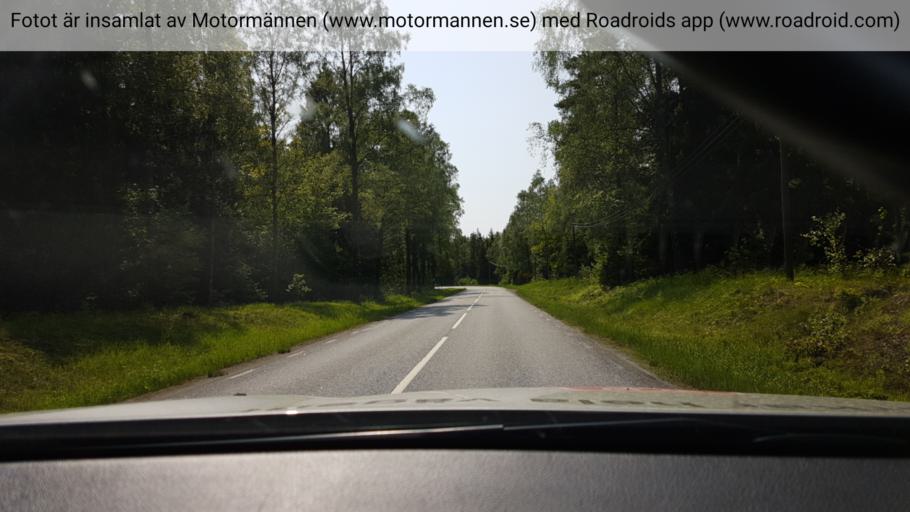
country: SE
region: Stockholm
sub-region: Haninge Kommun
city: Jordbro
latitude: 58.9948
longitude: 18.1075
